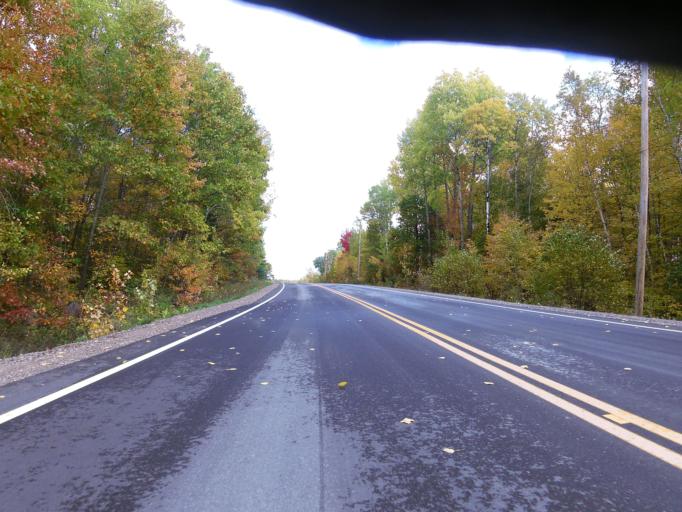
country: CA
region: Ontario
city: Petawawa
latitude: 45.8104
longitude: -77.3442
